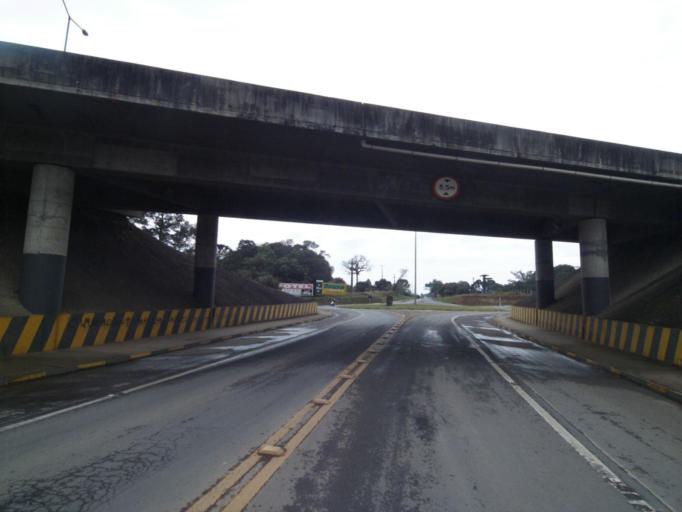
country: BR
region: Parana
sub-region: Irati
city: Irati
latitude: -25.4541
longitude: -50.6192
